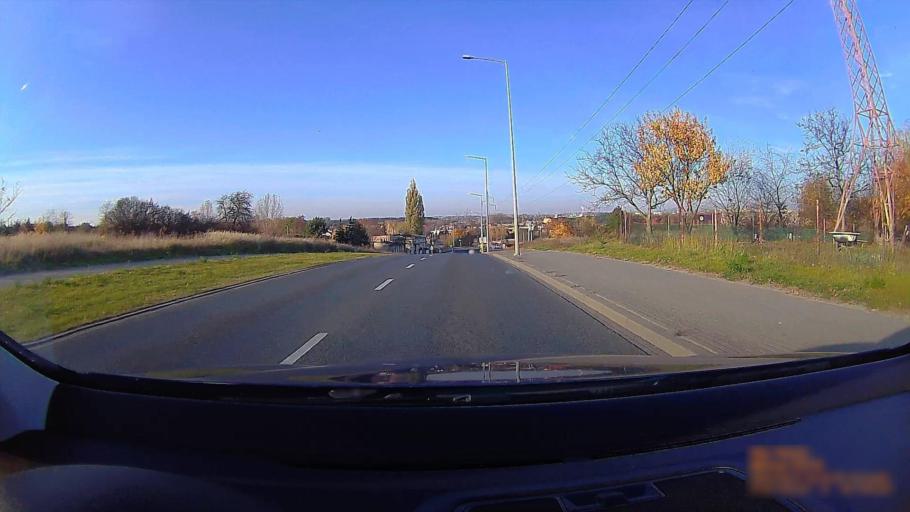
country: PL
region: Greater Poland Voivodeship
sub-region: Konin
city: Konin
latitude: 52.2016
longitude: 18.2335
